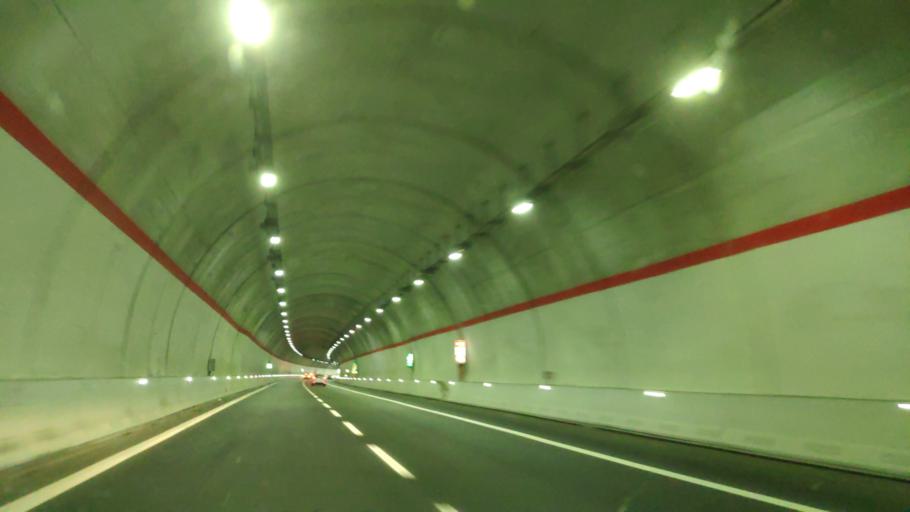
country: IT
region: Basilicate
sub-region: Provincia di Potenza
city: Lagonegro
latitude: 40.1119
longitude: 15.7899
